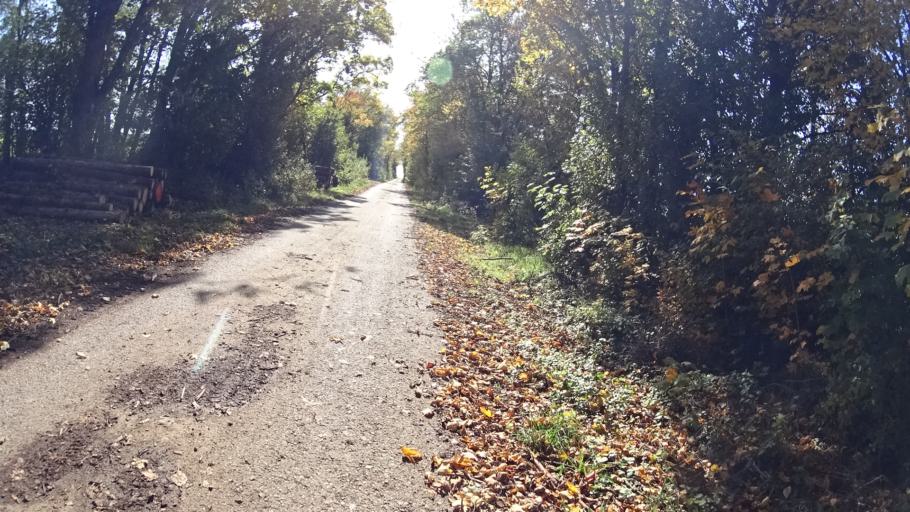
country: DE
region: Bavaria
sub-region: Upper Bavaria
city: Hitzhofen
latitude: 48.8638
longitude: 11.3333
